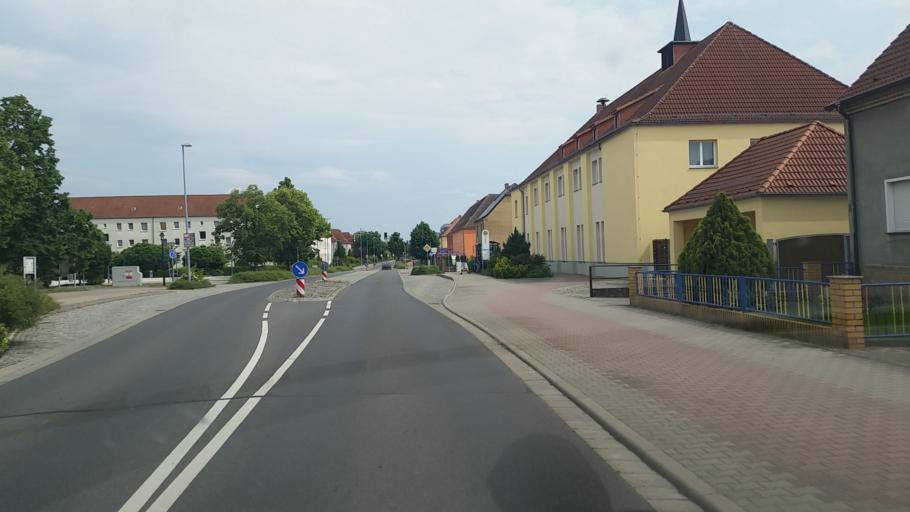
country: DE
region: Brandenburg
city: Schwarzheide
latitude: 51.4777
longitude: 13.8551
